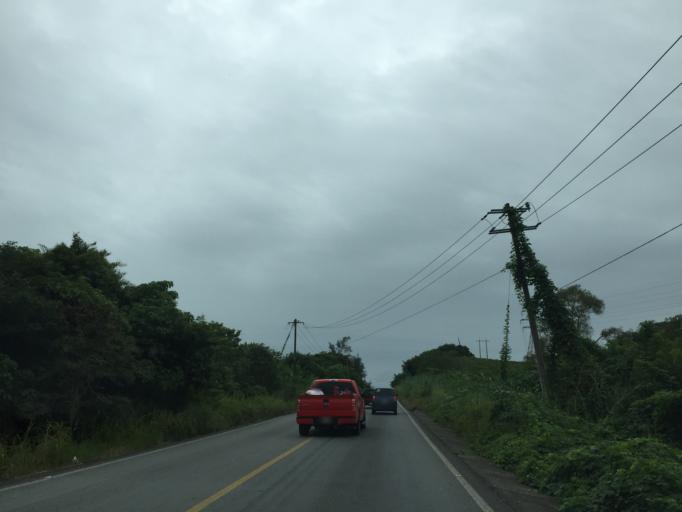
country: MX
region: Veracruz
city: Coatzintla
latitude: 20.4527
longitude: -97.4115
